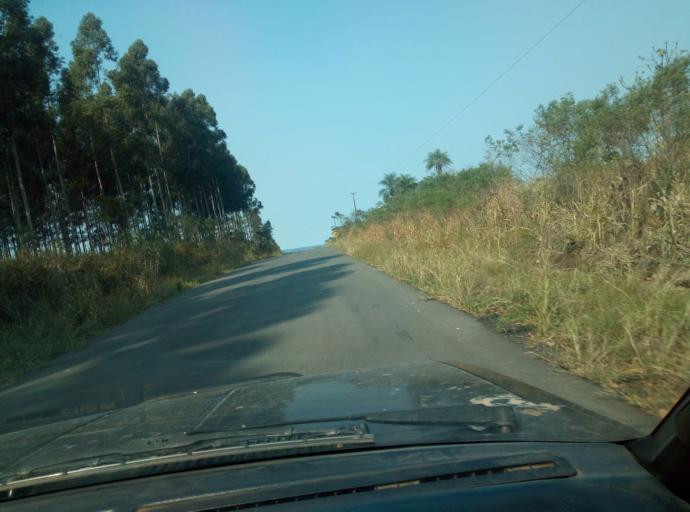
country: PY
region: Caaguazu
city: Carayao
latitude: -25.2490
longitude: -56.2880
